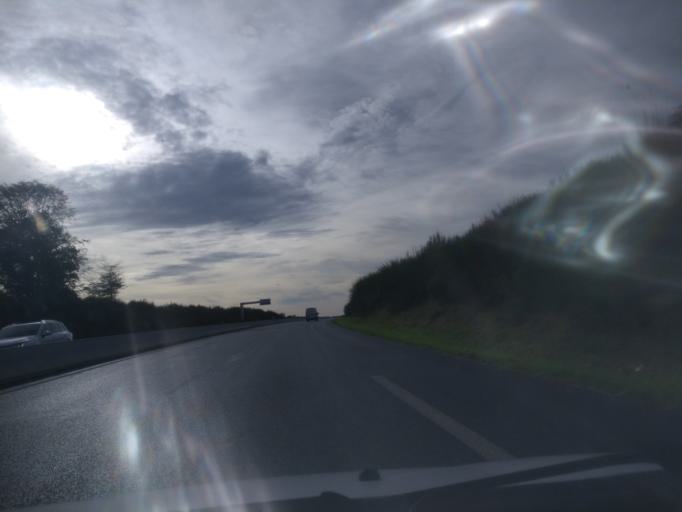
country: FR
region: Lower Normandy
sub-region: Departement de la Manche
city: Sartilly
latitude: 48.7551
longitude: -1.4447
